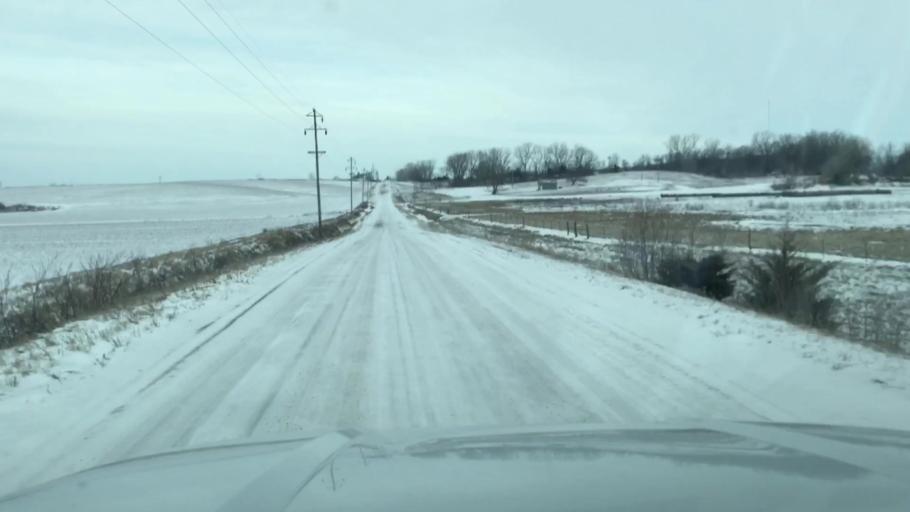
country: US
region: Missouri
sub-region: Holt County
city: Oregon
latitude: 40.1301
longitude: -95.0523
